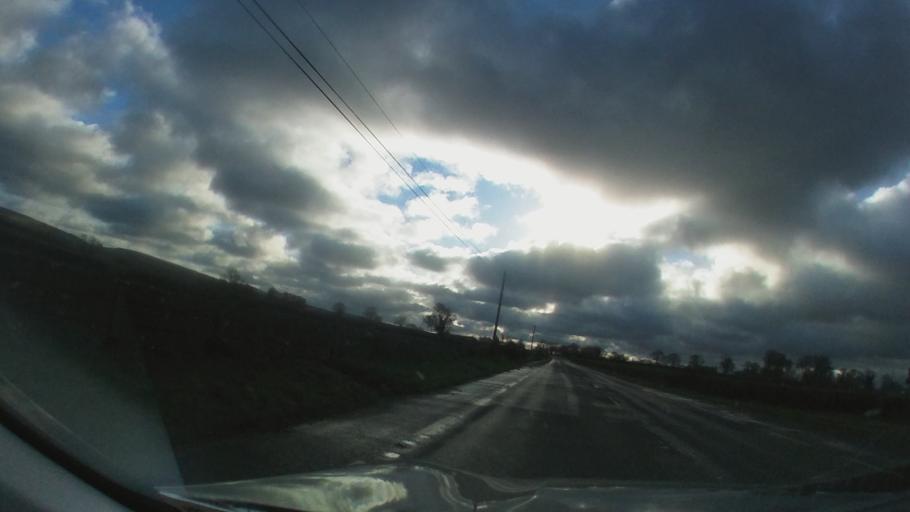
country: IE
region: Leinster
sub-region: Kilkenny
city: Thomastown
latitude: 52.5961
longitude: -7.0943
